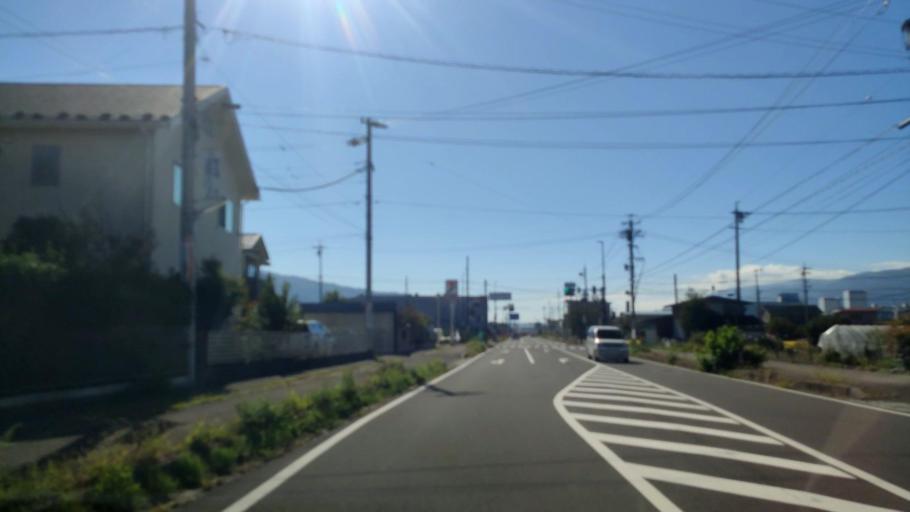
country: JP
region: Nagano
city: Suwa
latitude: 36.0368
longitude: 138.1079
